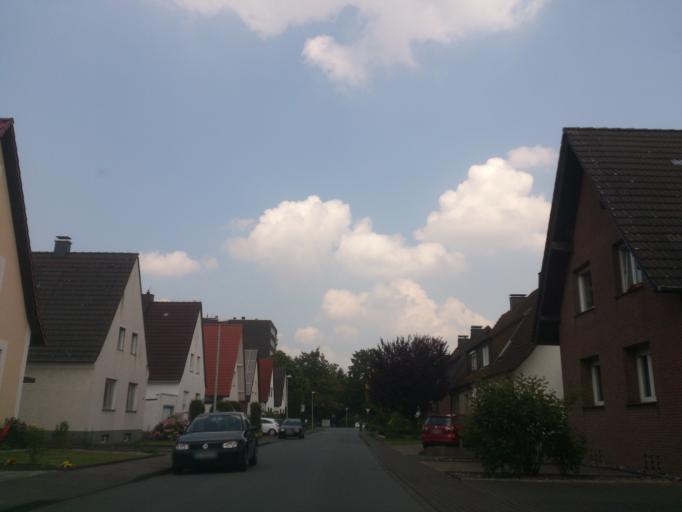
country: DE
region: North Rhine-Westphalia
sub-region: Regierungsbezirk Detmold
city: Paderborn
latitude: 51.7145
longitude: 8.7222
